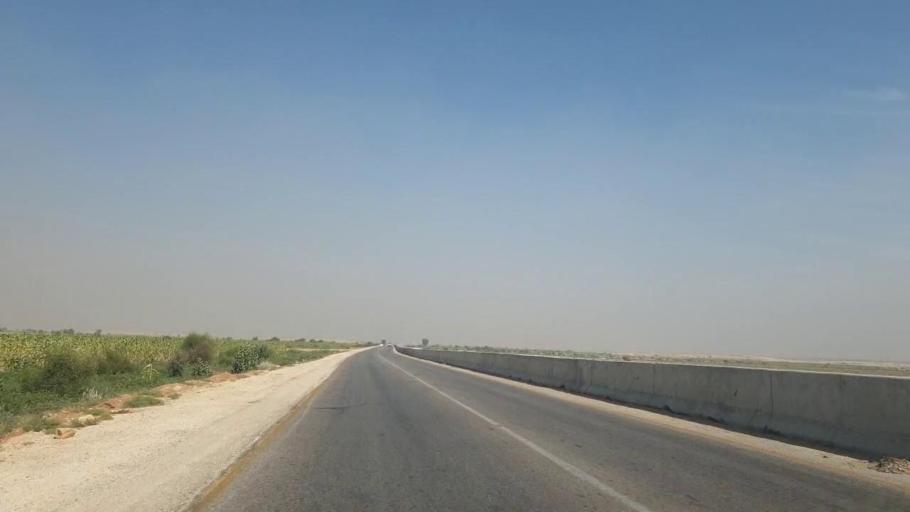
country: PK
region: Sindh
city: Jamshoro
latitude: 25.5416
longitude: 68.2894
